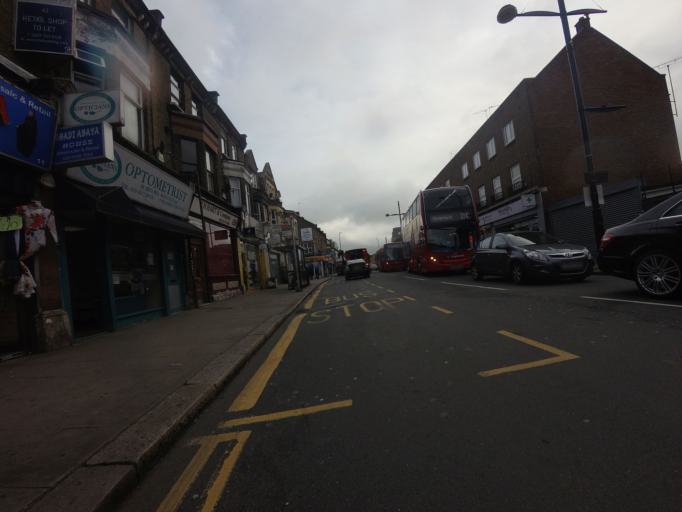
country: GB
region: England
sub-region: Greater London
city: East Ham
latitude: 51.5374
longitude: 0.0349
